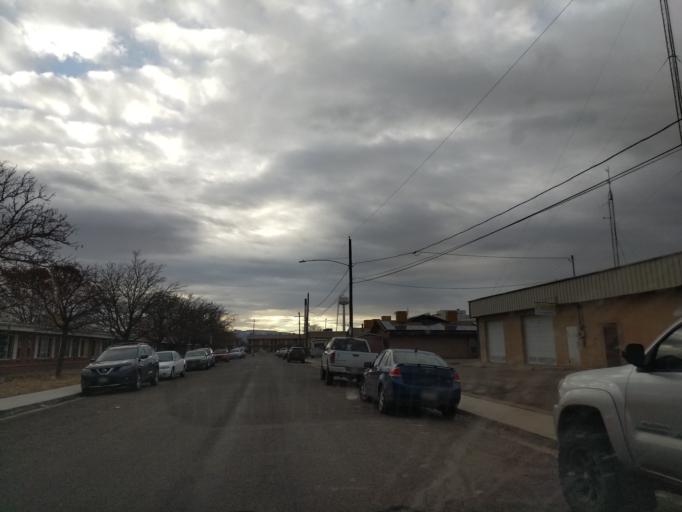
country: US
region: Colorado
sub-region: Mesa County
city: Grand Junction
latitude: 39.0751
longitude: -108.5360
